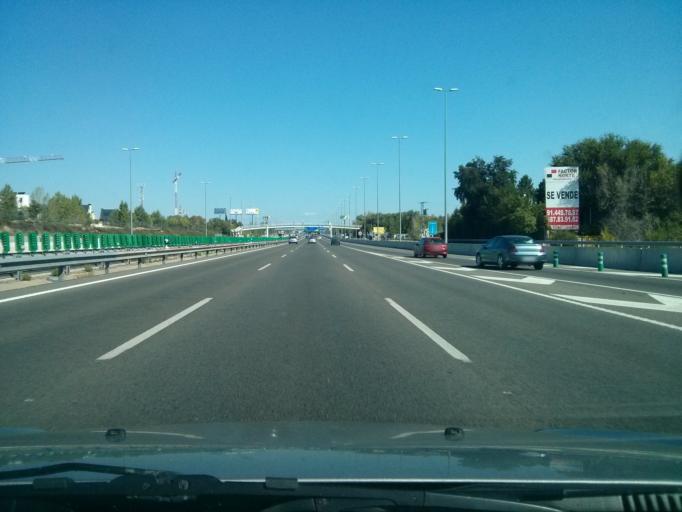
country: ES
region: Madrid
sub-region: Provincia de Madrid
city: San Sebastian de los Reyes
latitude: 40.5939
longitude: -3.5820
